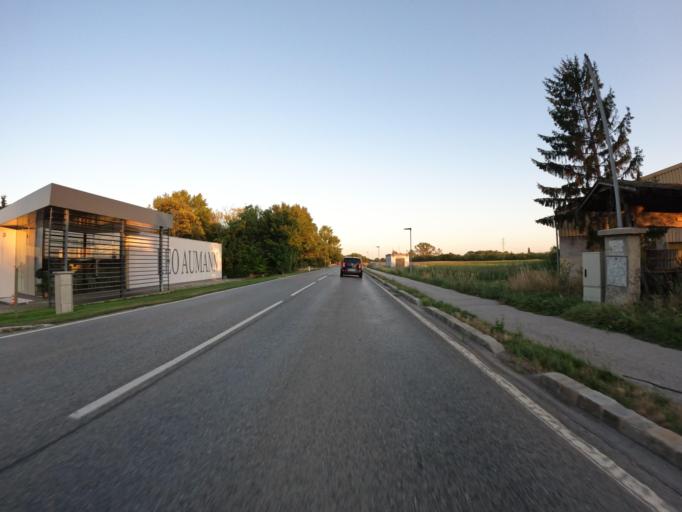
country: AT
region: Lower Austria
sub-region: Politischer Bezirk Baden
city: Pfaffstatten
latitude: 47.9991
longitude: 16.2701
